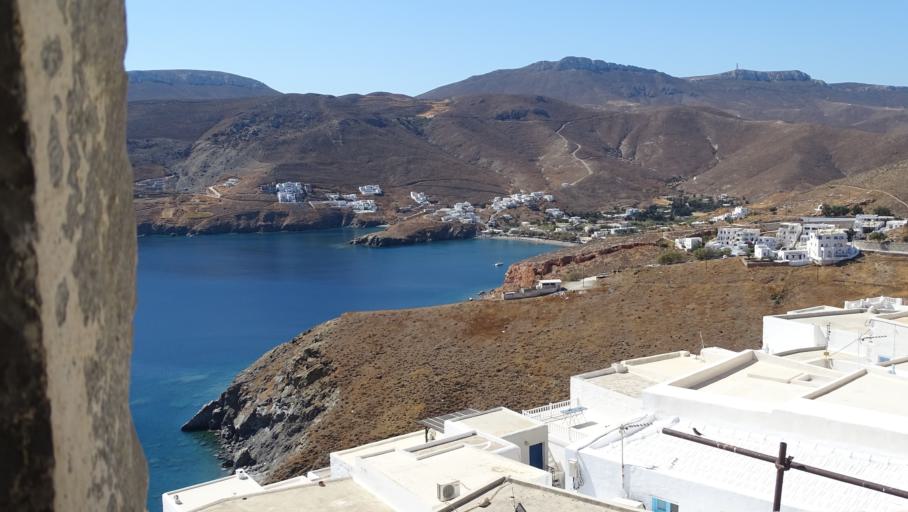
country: GR
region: South Aegean
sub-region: Nomos Dodekanisou
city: Astypalaia
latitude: 36.5437
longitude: 26.3555
